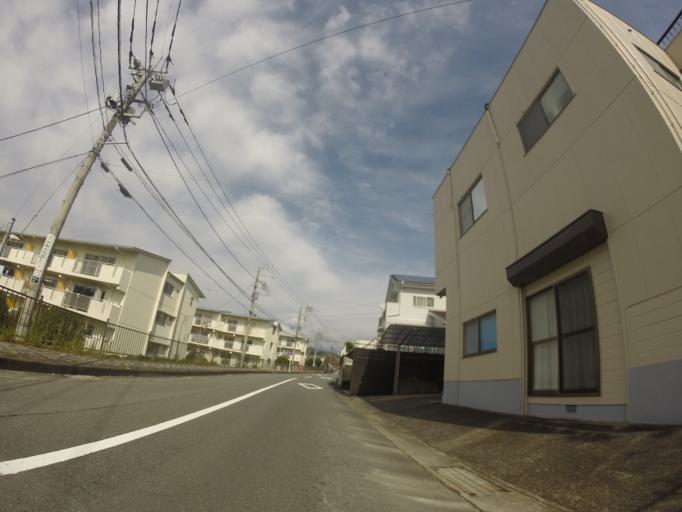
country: JP
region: Shizuoka
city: Fuji
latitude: 35.1832
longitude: 138.6908
